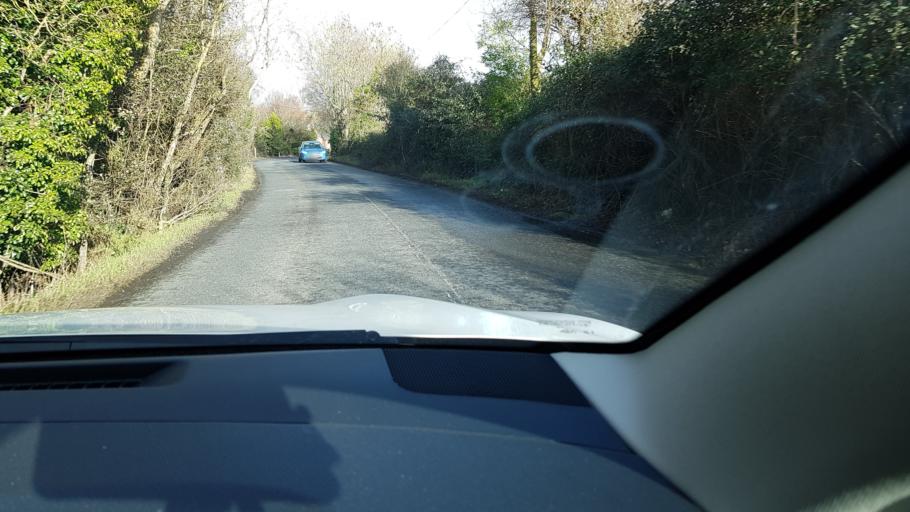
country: IE
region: Leinster
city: Lucan
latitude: 53.3734
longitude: -6.4426
